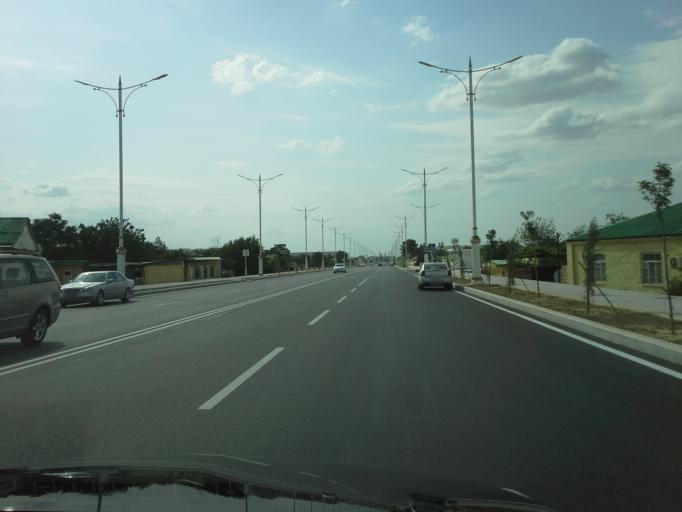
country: TM
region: Ahal
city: Ashgabat
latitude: 37.9590
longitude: 58.3388
